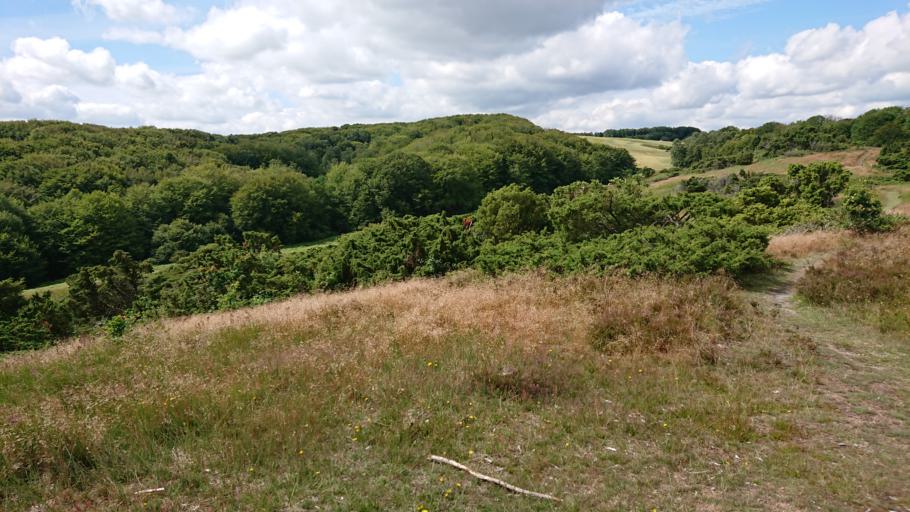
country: DK
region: North Denmark
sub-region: Hjorring Kommune
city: Sindal
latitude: 57.4524
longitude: 10.3375
